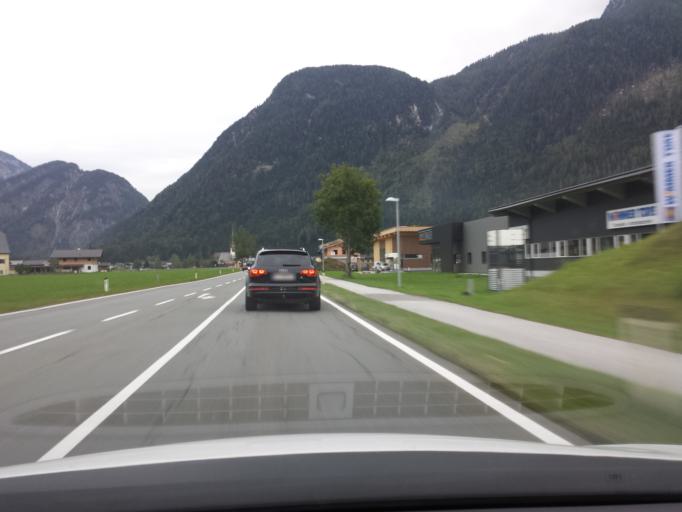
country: AT
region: Salzburg
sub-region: Politischer Bezirk Zell am See
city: Sankt Martin bei Lofer
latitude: 47.5728
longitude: 12.7013
